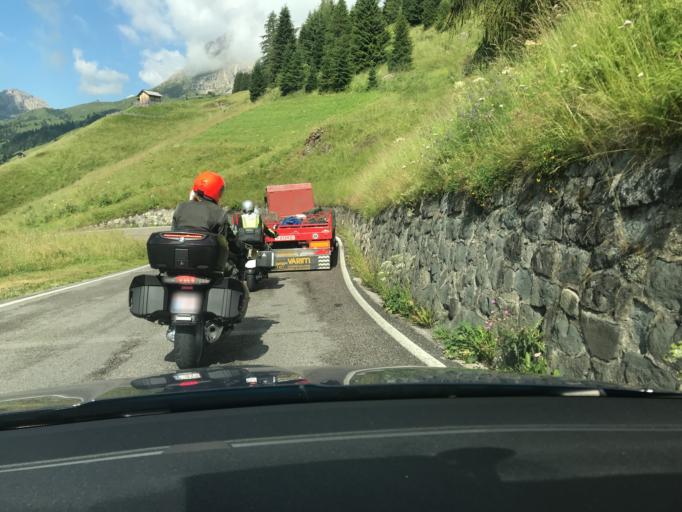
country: IT
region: Trentino-Alto Adige
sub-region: Bolzano
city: Corvara in Badia
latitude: 46.5012
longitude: 11.8849
